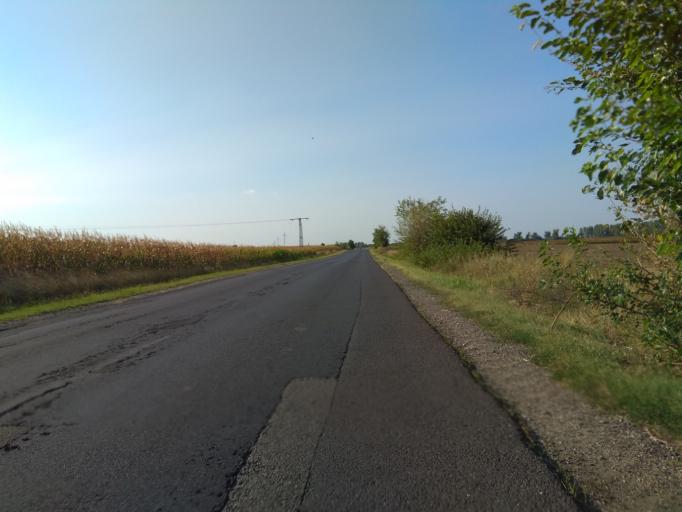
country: HU
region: Borsod-Abauj-Zemplen
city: Onod
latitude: 48.0149
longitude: 20.9077
